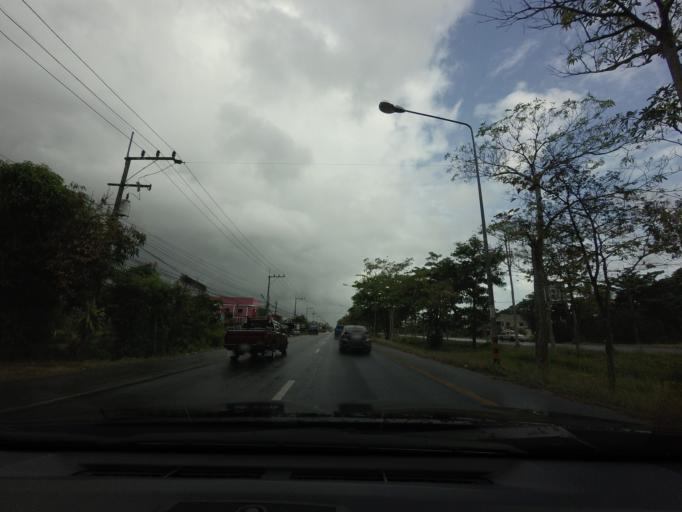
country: TH
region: Pattani
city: Nong Chik
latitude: 6.8021
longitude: 101.1478
